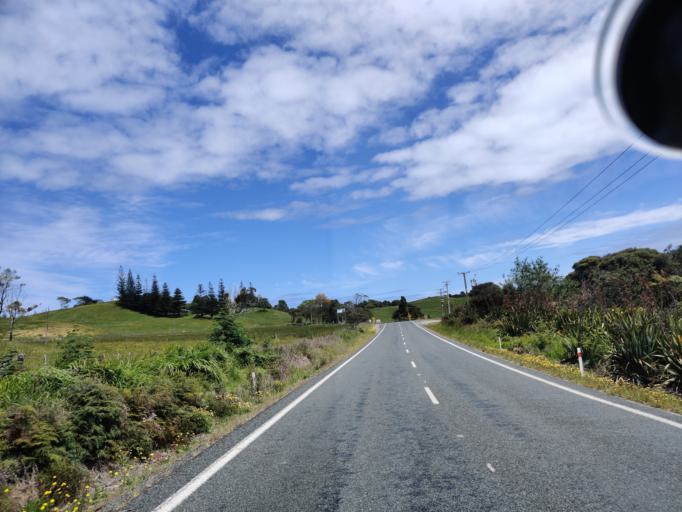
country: NZ
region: Northland
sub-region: Far North District
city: Kaitaia
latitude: -35.0106
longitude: 173.2031
